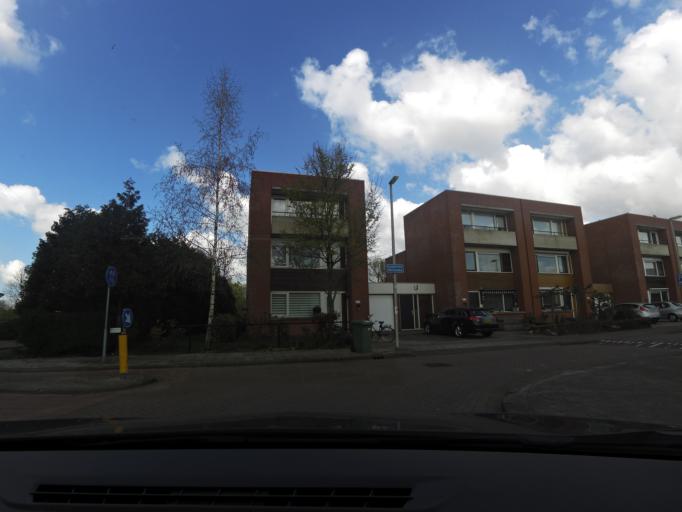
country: NL
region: South Holland
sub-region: Gemeente Spijkenisse
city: Spijkenisse
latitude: 51.8679
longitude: 4.3681
